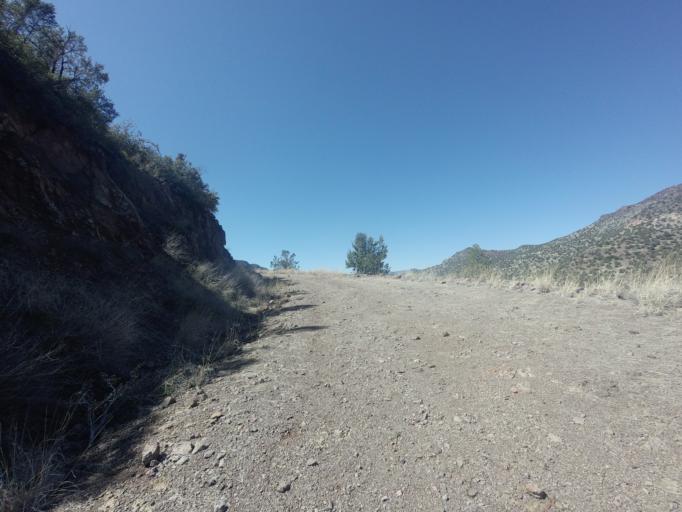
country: US
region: Arizona
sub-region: Gila County
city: Pine
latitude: 34.4074
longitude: -111.6053
